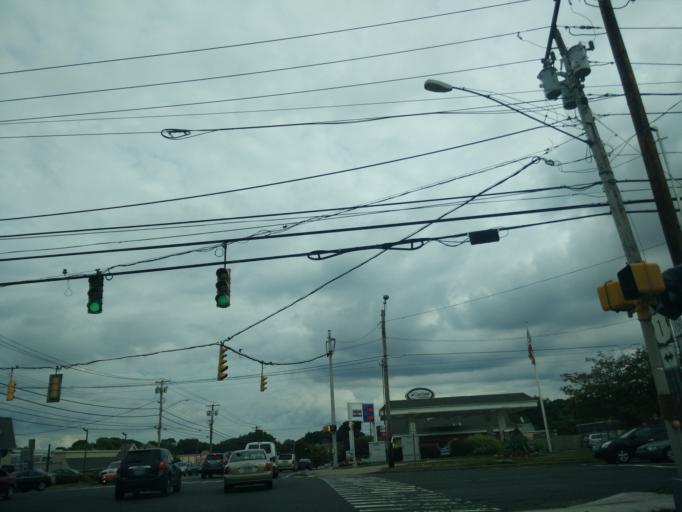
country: US
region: Connecticut
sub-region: Fairfield County
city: Stratford
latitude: 41.1989
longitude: -73.1320
